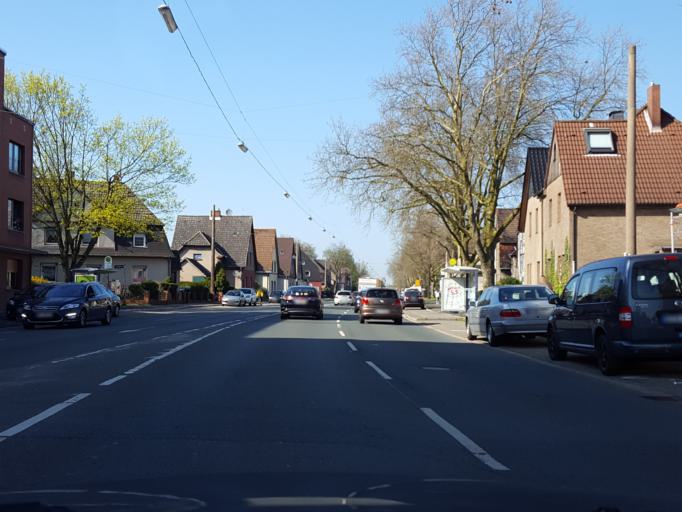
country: DE
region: North Rhine-Westphalia
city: Castrop-Rauxel
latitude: 51.5845
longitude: 7.3099
